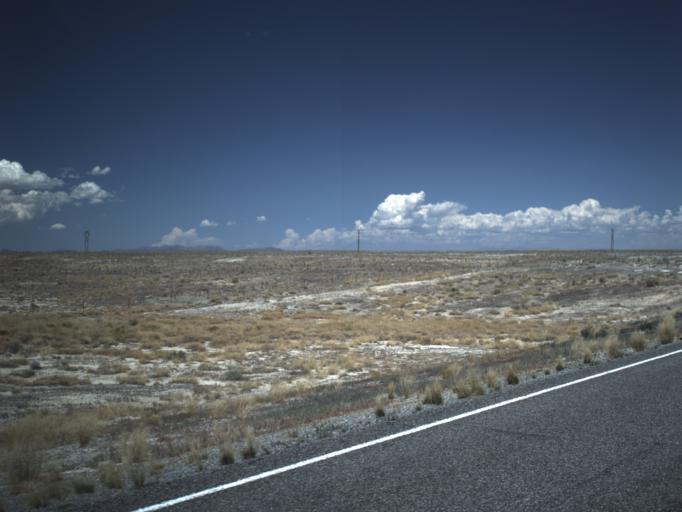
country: US
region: Utah
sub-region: Millard County
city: Delta
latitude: 39.1678
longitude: -113.0391
